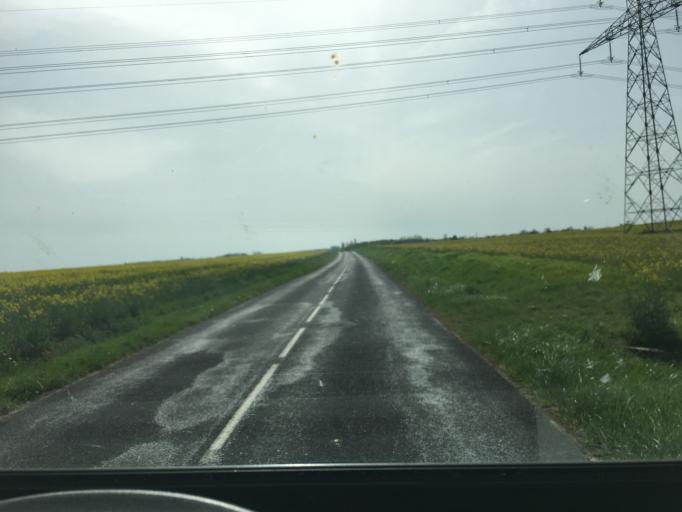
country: FR
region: Lorraine
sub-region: Departement de Meurthe-et-Moselle
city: Fleville-devant-Nancy
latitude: 48.6237
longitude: 6.2233
